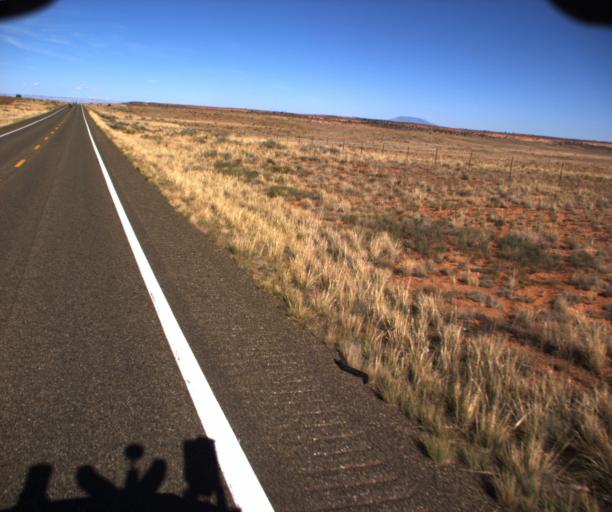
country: US
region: Arizona
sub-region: Coconino County
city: LeChee
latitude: 36.7627
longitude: -111.5654
